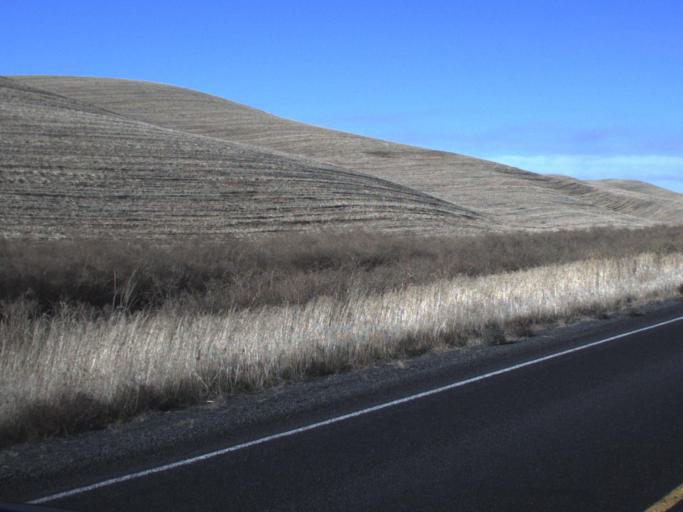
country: US
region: Washington
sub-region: Walla Walla County
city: Walla Walla
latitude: 46.2371
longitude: -118.3696
